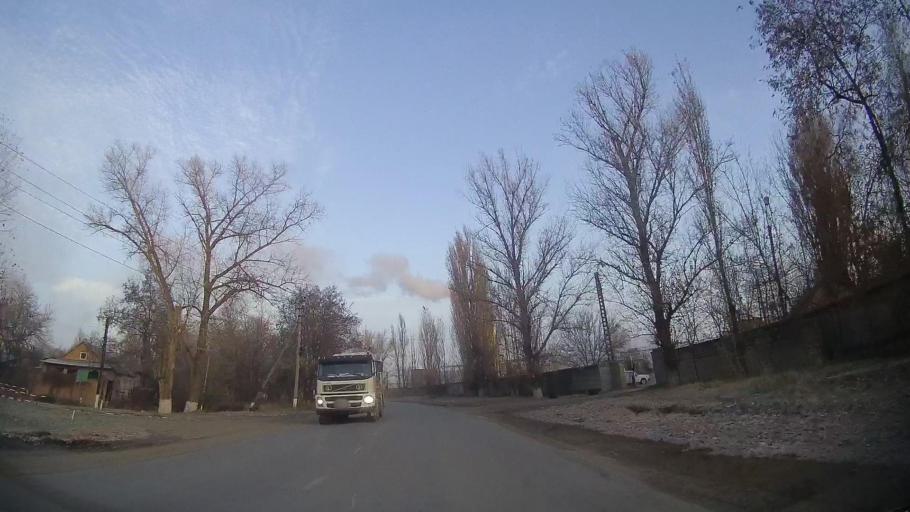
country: RU
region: Rostov
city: Bataysk
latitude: 47.1003
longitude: 39.7619
